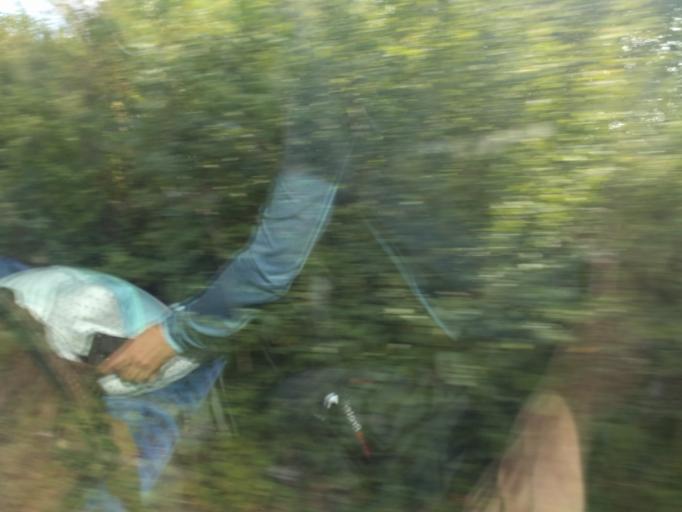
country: DE
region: Schleswig-Holstein
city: Heidekamp
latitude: 53.8389
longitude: 10.5148
